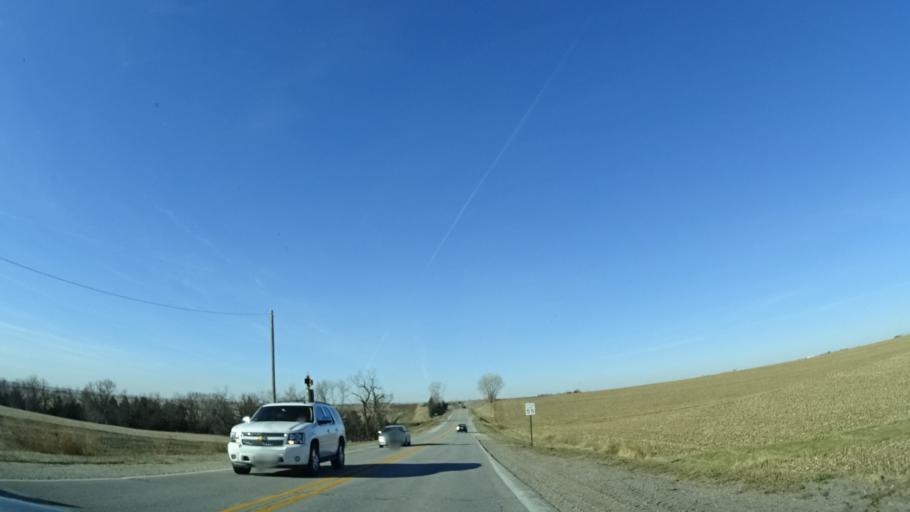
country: US
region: Nebraska
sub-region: Sarpy County
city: Springfield
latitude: 41.0889
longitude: -96.0813
